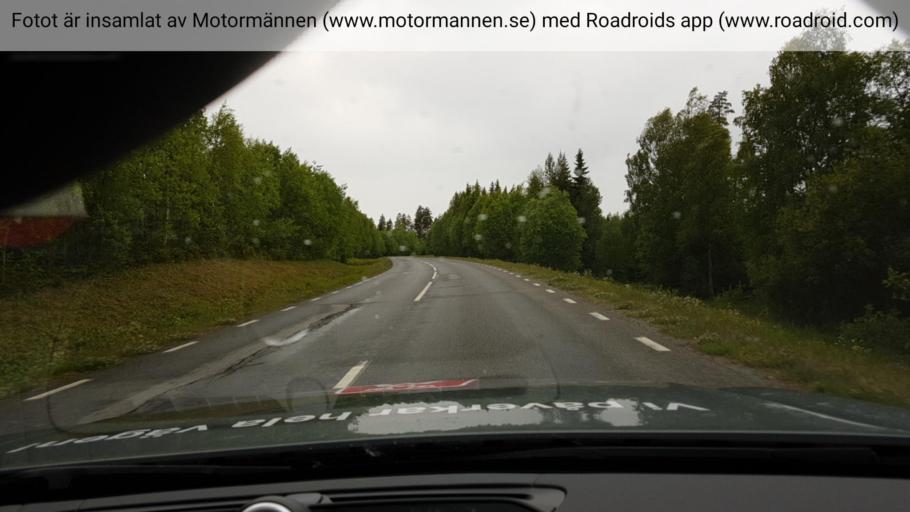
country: SE
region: Jaemtland
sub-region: Stroemsunds Kommun
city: Stroemsund
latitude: 63.5971
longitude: 15.3201
